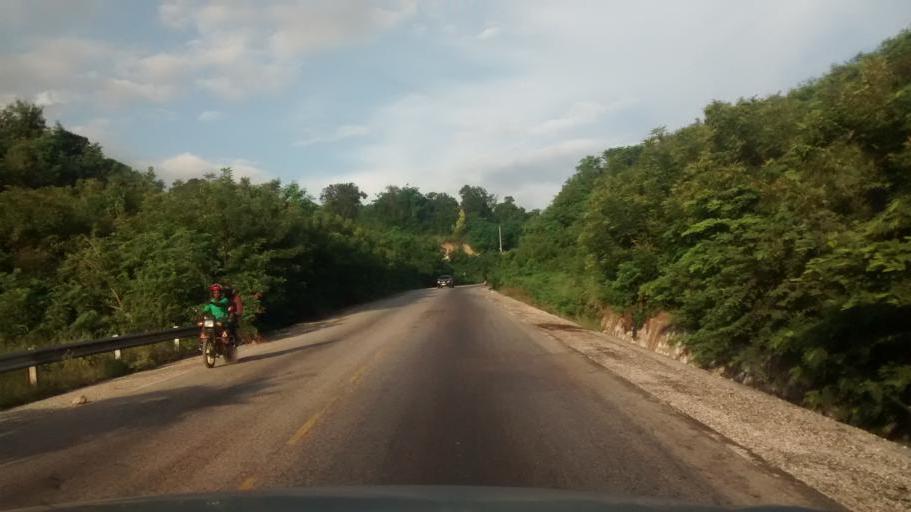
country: HT
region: Ouest
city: Grangwav
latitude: 18.4198
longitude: -72.8039
